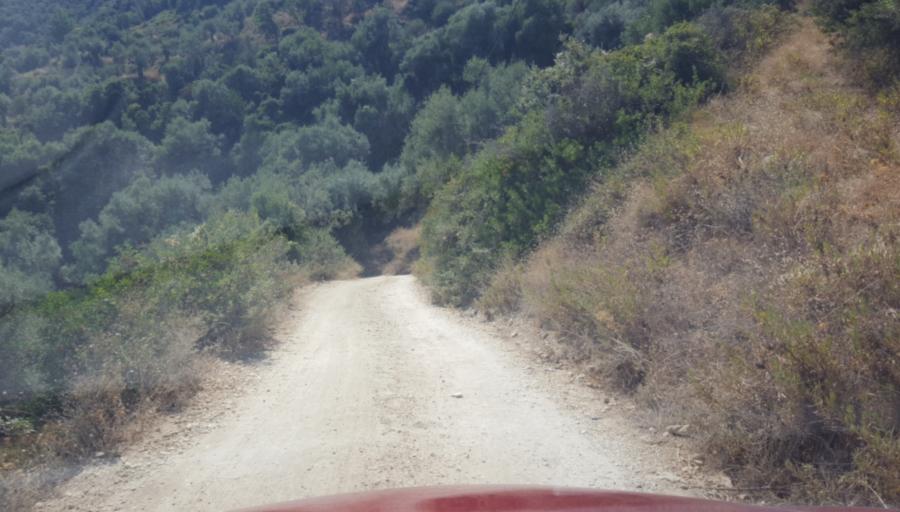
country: GR
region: Ionian Islands
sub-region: Lefkada
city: Nidri
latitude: 38.6708
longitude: 20.7117
